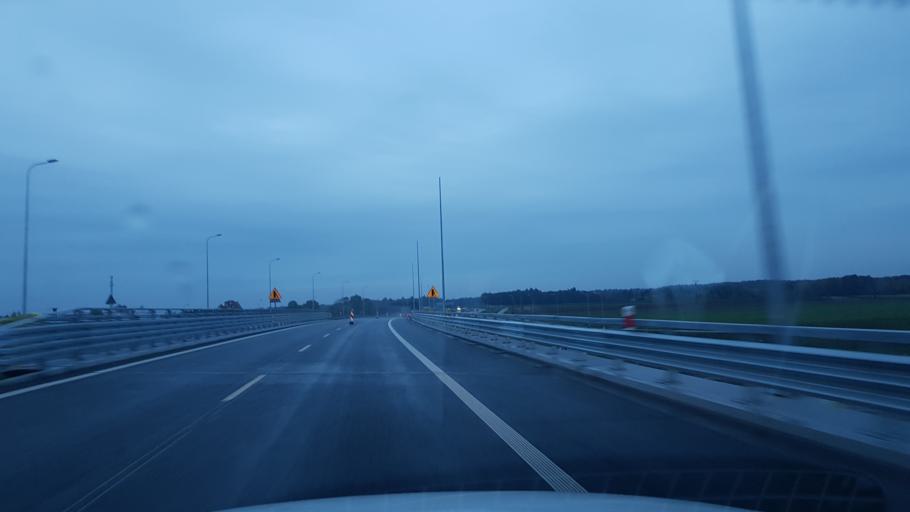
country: PL
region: West Pomeranian Voivodeship
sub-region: Powiat gryficki
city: Ploty
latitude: 53.8181
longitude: 15.2534
